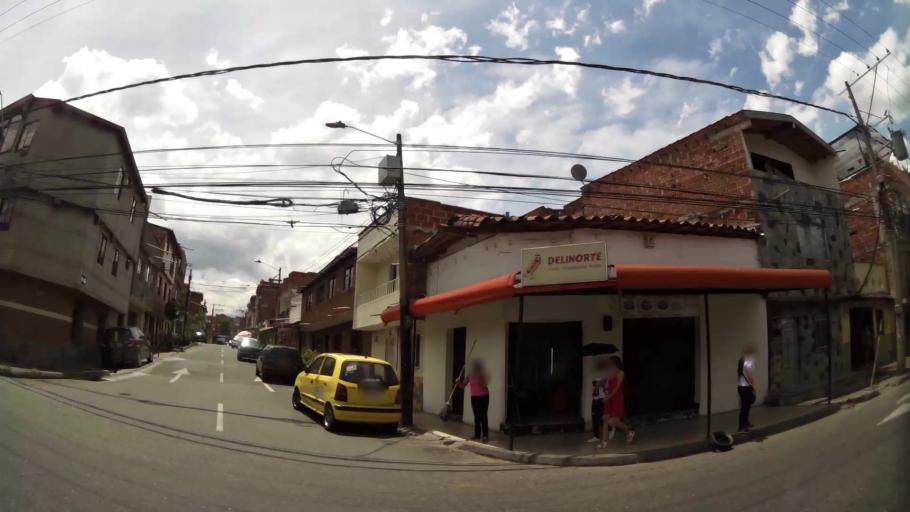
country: CO
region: Antioquia
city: Bello
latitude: 6.3422
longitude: -75.5616
